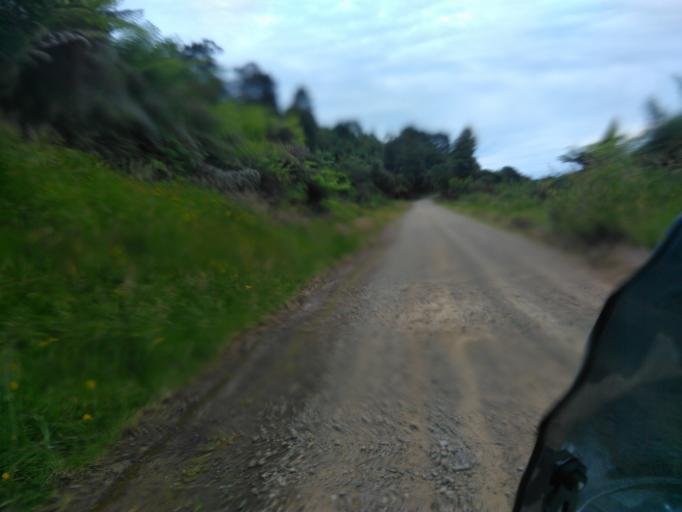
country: NZ
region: Bay of Plenty
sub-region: Opotiki District
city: Opotiki
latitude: -38.0273
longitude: 177.4401
